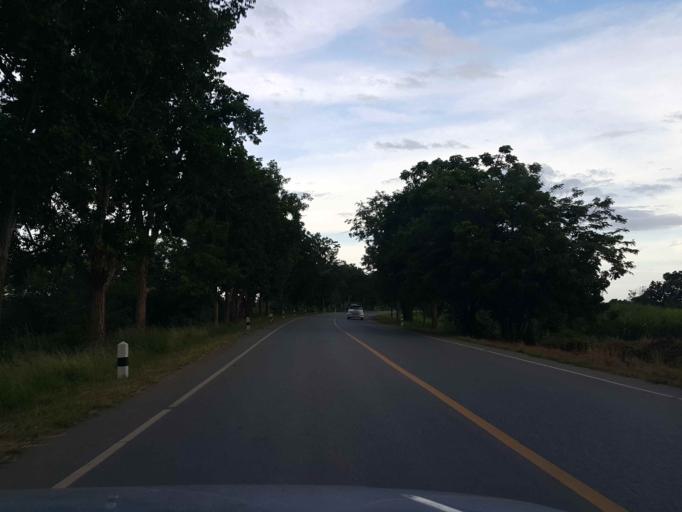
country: TH
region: Sukhothai
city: Sawankhalok
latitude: 17.3721
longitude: 99.7408
